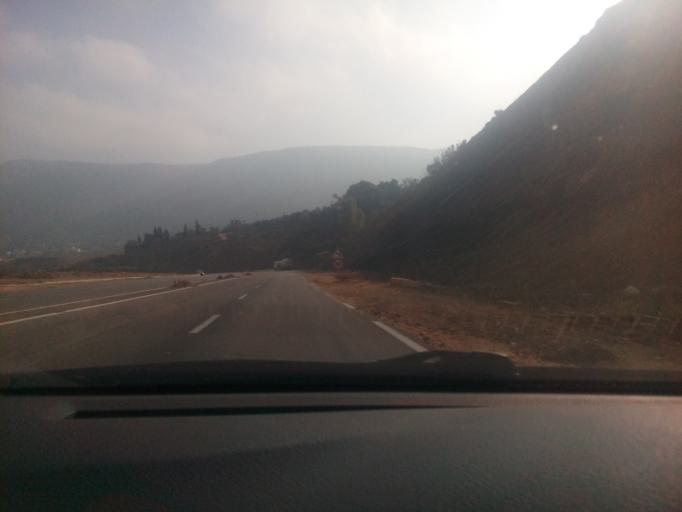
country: DZ
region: Oran
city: Mers el Kebir
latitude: 35.7141
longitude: -0.7000
